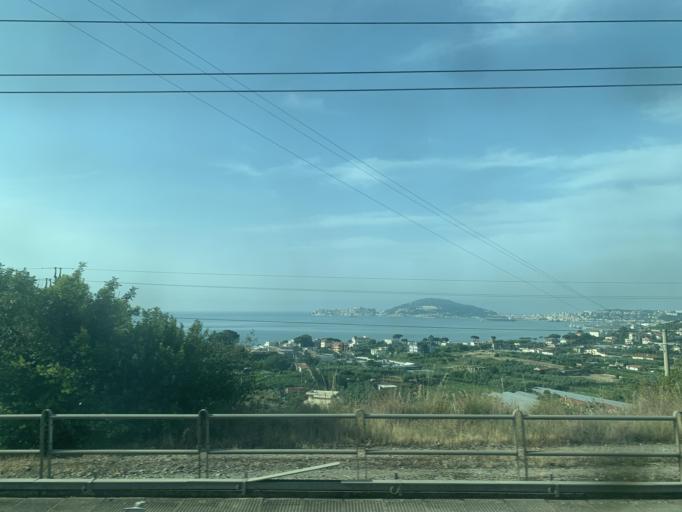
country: IT
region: Latium
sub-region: Provincia di Latina
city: Gaeta
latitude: 41.2536
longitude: 13.5822
